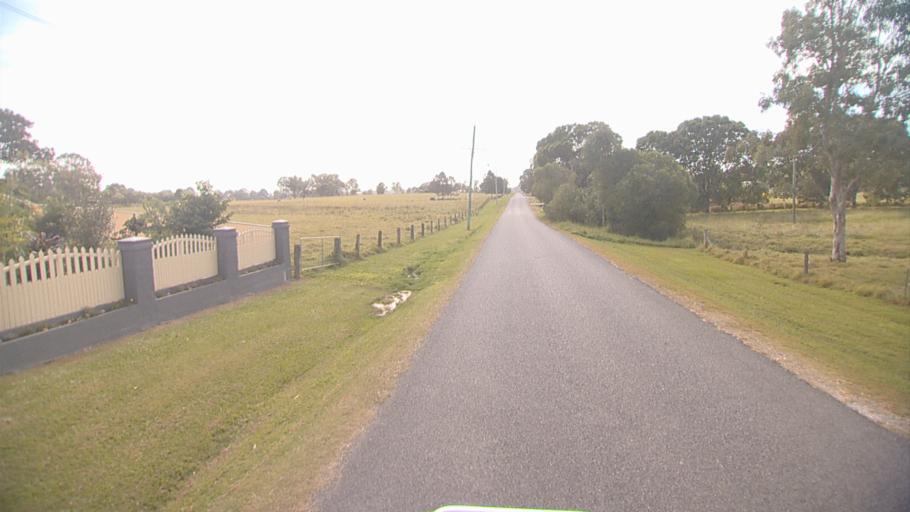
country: AU
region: Queensland
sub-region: Logan
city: Waterford West
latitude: -27.6820
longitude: 153.1585
